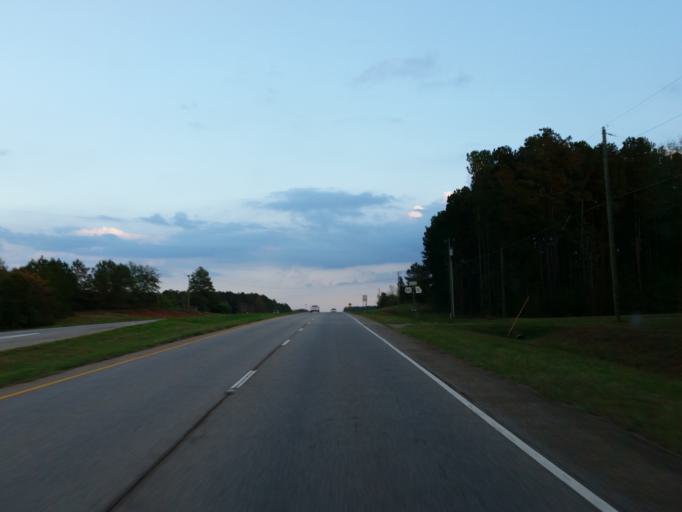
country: US
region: Georgia
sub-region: Pulaski County
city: Hawkinsville
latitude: 32.3592
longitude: -83.5960
